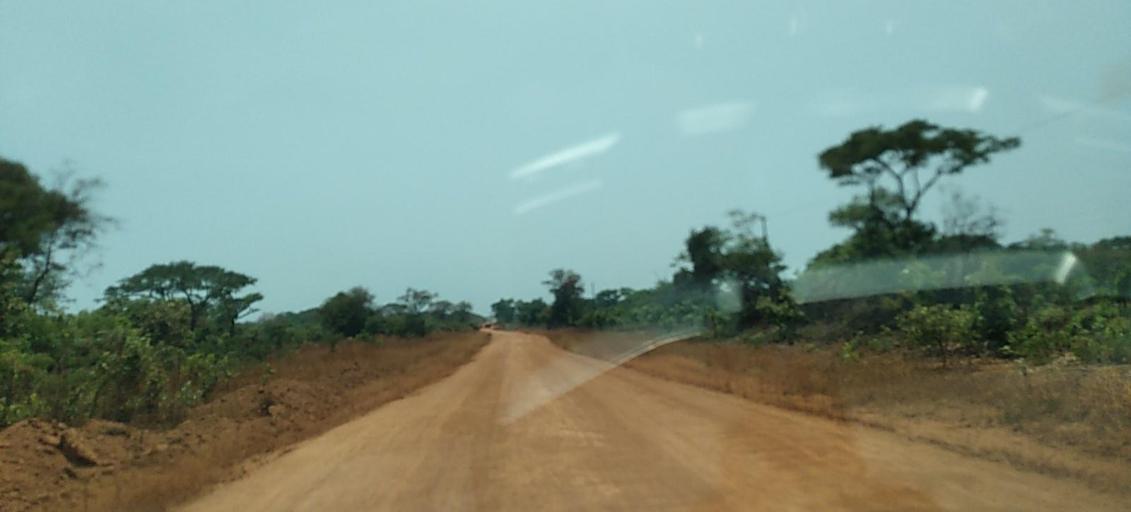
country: CD
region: Katanga
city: Kipushi
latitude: -11.9276
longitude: 26.9956
